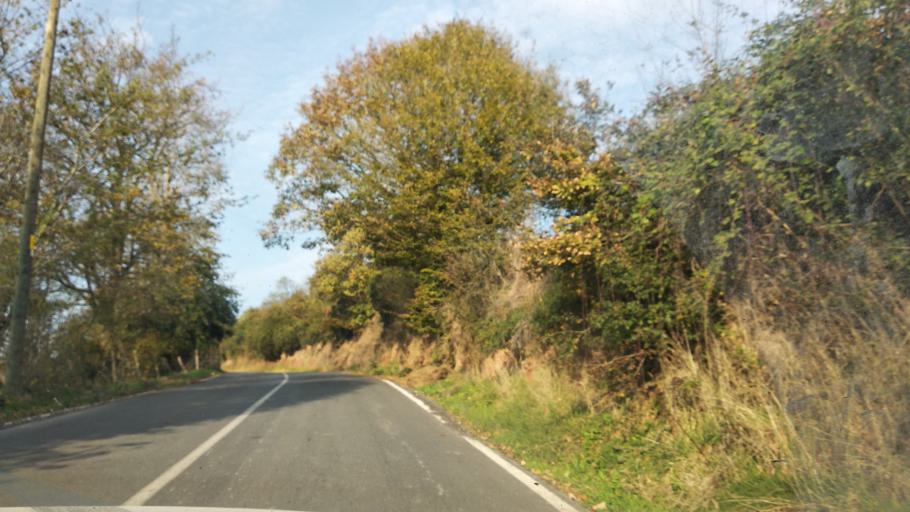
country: TR
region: Sakarya
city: Karasu
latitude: 41.0619
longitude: 30.6179
